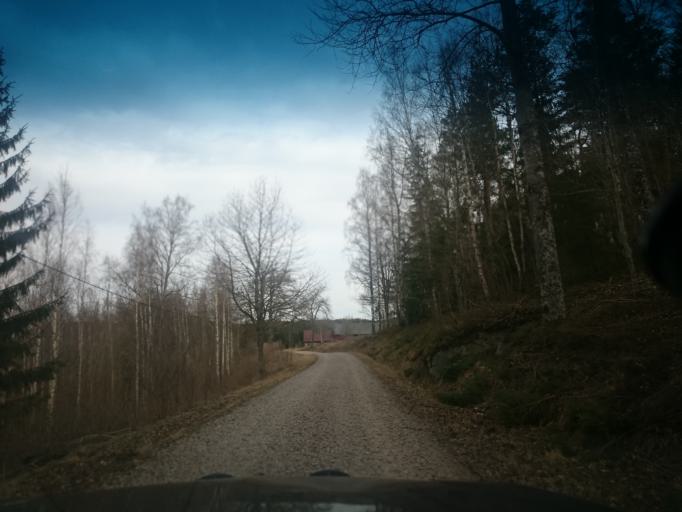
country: SE
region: Joenkoeping
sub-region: Vetlanda Kommun
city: Vetlanda
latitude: 57.3326
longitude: 15.1570
